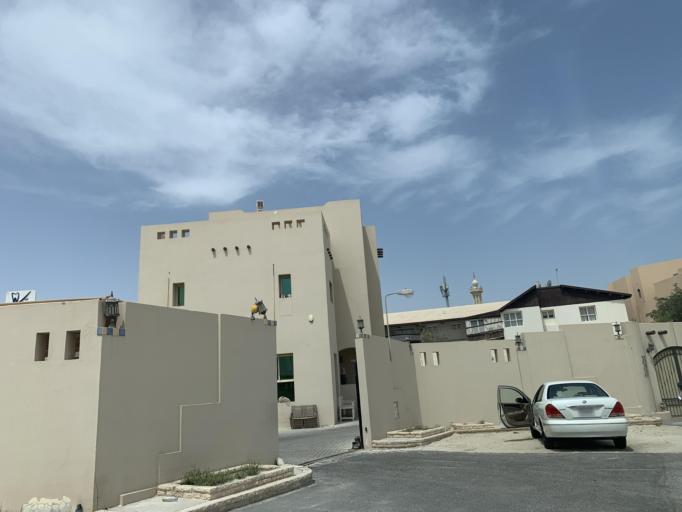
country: BH
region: Northern
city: Ar Rifa'
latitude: 26.1426
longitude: 50.5605
